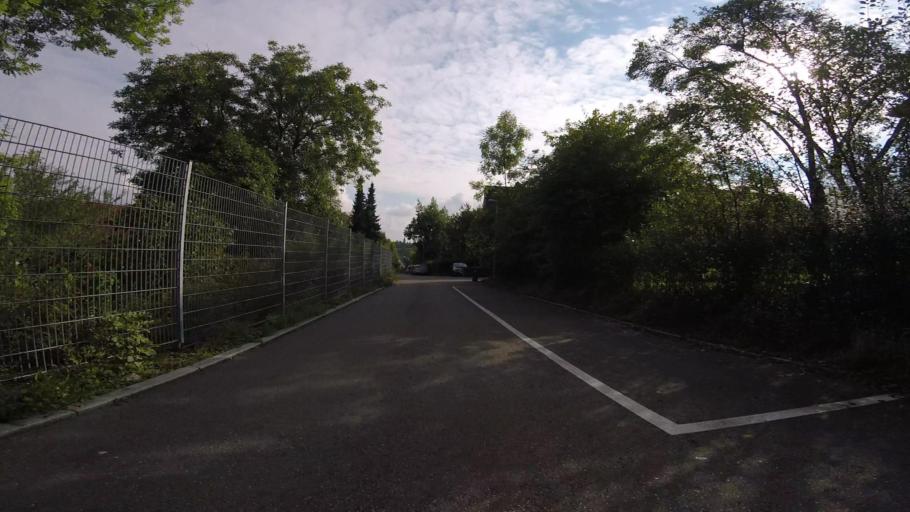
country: DE
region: Baden-Wuerttemberg
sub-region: Regierungsbezirk Stuttgart
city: Backnang
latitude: 48.9494
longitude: 9.4244
